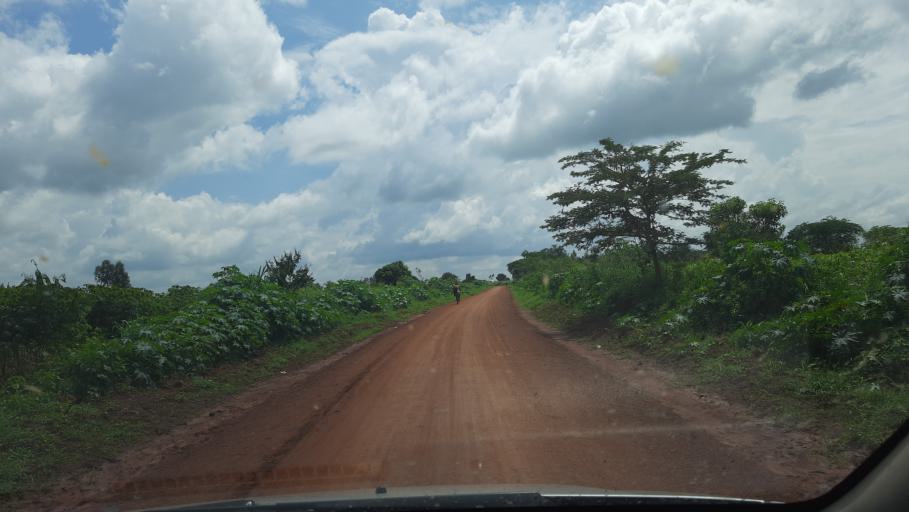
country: UG
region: Western Region
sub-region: Kiryandongo District
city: Kiryandongo
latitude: 1.8240
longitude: 31.9827
